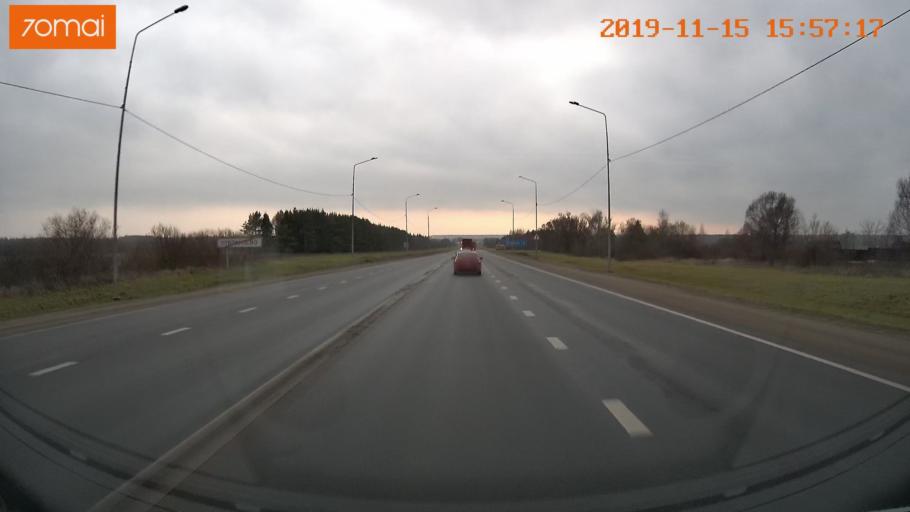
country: RU
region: Jaroslavl
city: Yaroslavl
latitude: 57.8320
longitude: 39.9650
